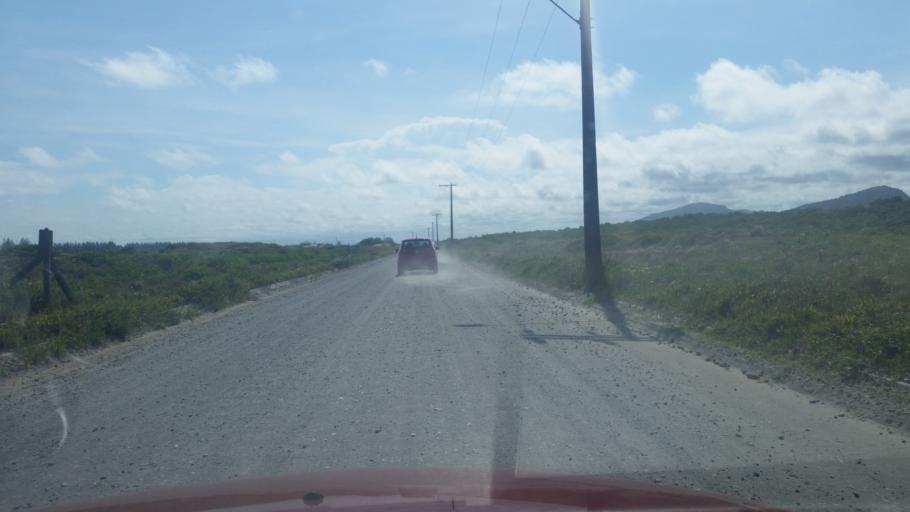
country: BR
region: Sao Paulo
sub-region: Iguape
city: Iguape
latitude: -24.7018
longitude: -47.4647
